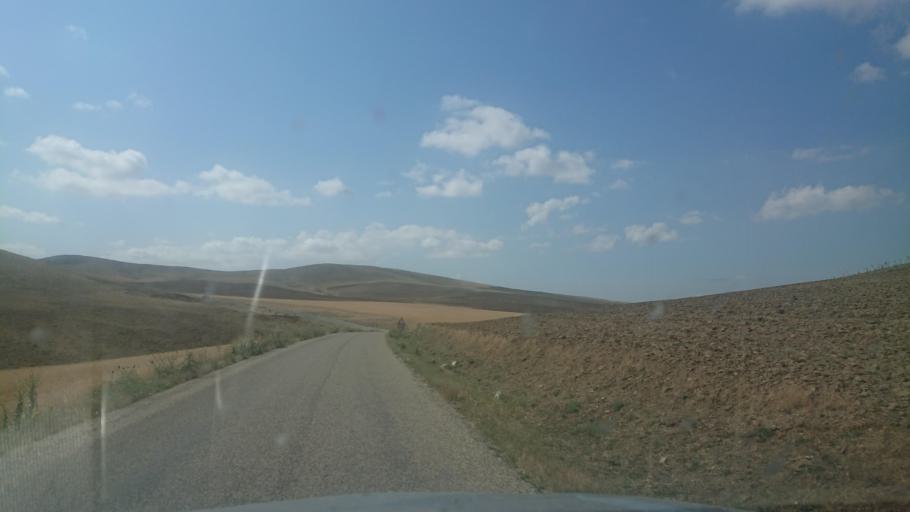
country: TR
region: Aksaray
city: Sariyahsi
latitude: 39.0093
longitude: 33.9494
